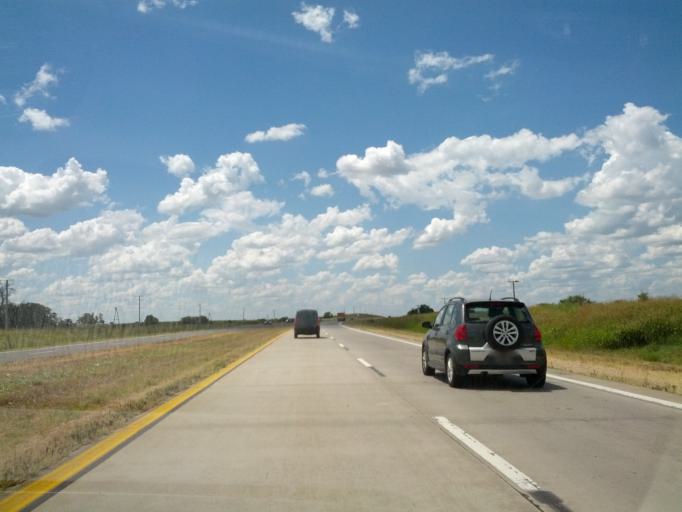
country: AR
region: Entre Rios
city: Gualeguaychu
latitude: -32.9197
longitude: -58.5662
